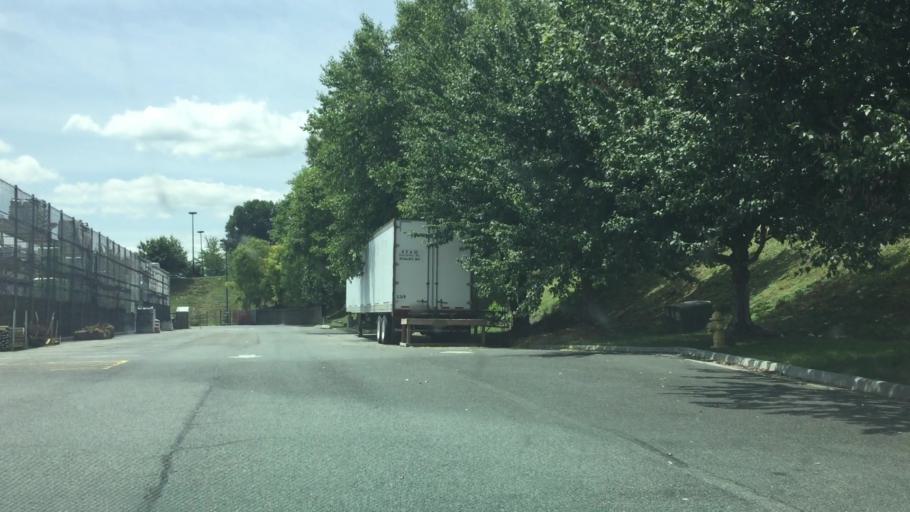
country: US
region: Virginia
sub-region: Wythe County
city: Wytheville
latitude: 36.9584
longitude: -81.1021
